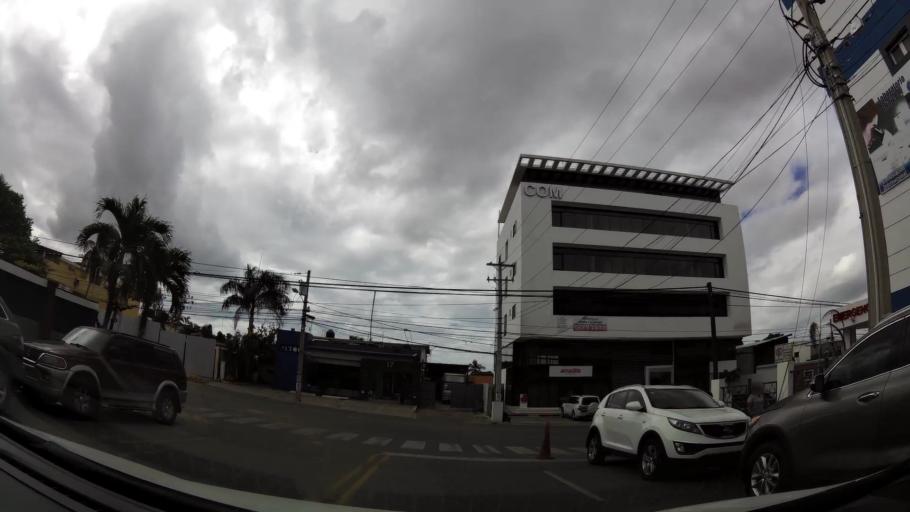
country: DO
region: Nacional
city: Bella Vista
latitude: 18.4760
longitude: -69.9573
